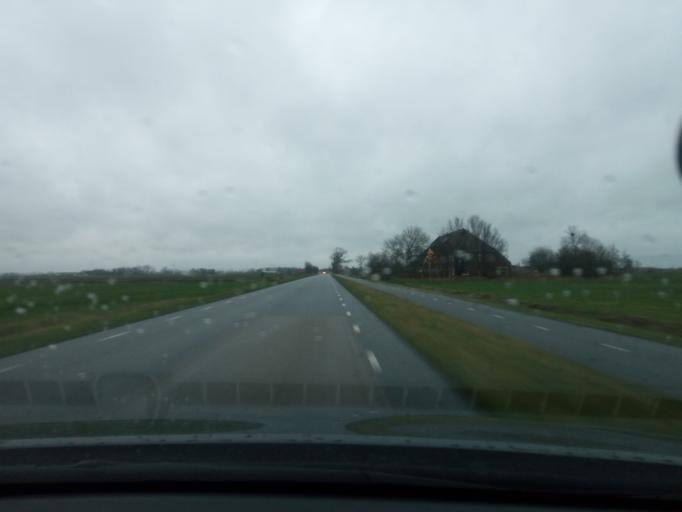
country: NL
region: Groningen
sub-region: Gemeente Winsum
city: Winsum
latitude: 53.3376
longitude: 6.5507
